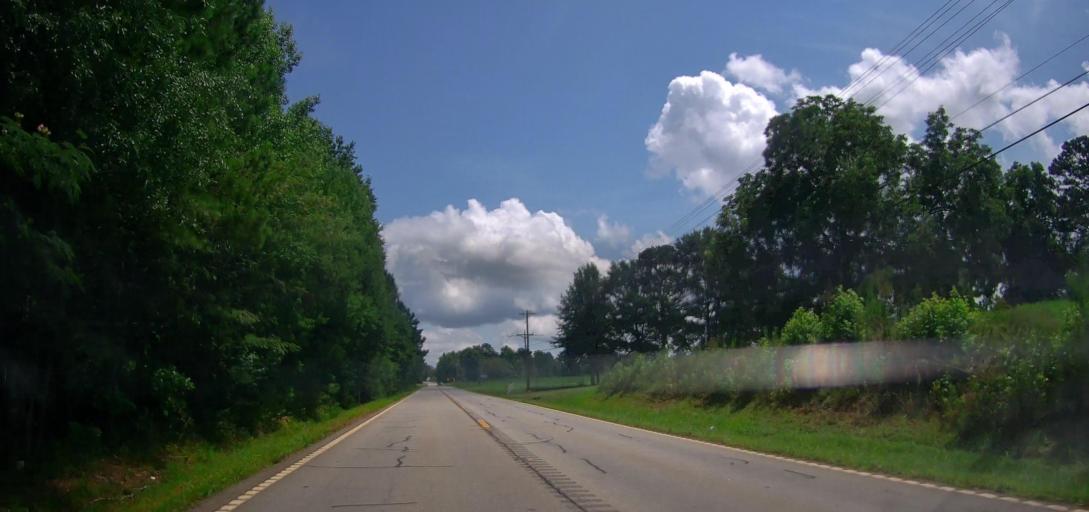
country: US
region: Georgia
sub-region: Carroll County
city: Bowdon
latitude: 33.3890
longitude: -85.2514
